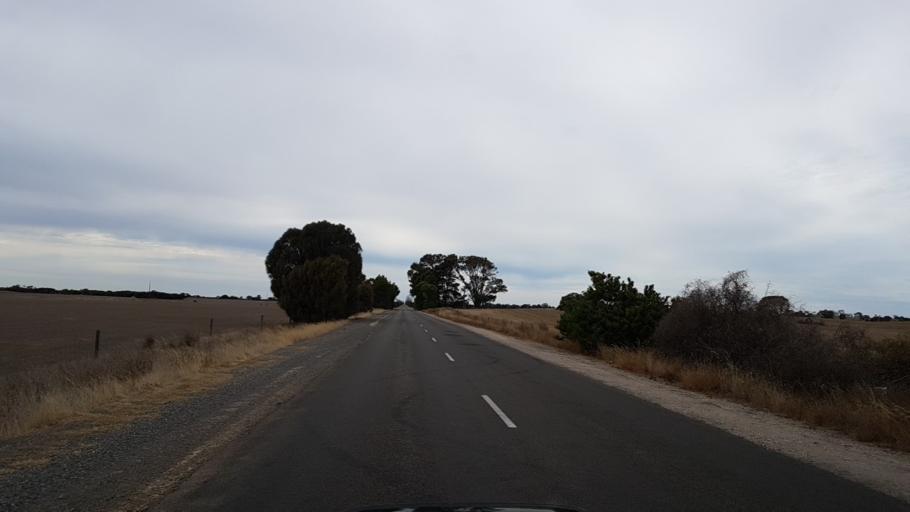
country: AU
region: South Australia
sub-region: Yorke Peninsula
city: Honiton
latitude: -34.9851
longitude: 137.1849
